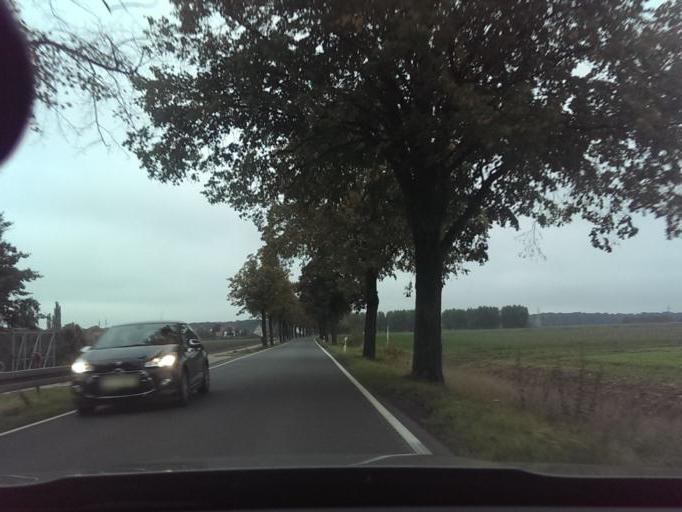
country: DE
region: Lower Saxony
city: Seelze
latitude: 52.3726
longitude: 9.5664
